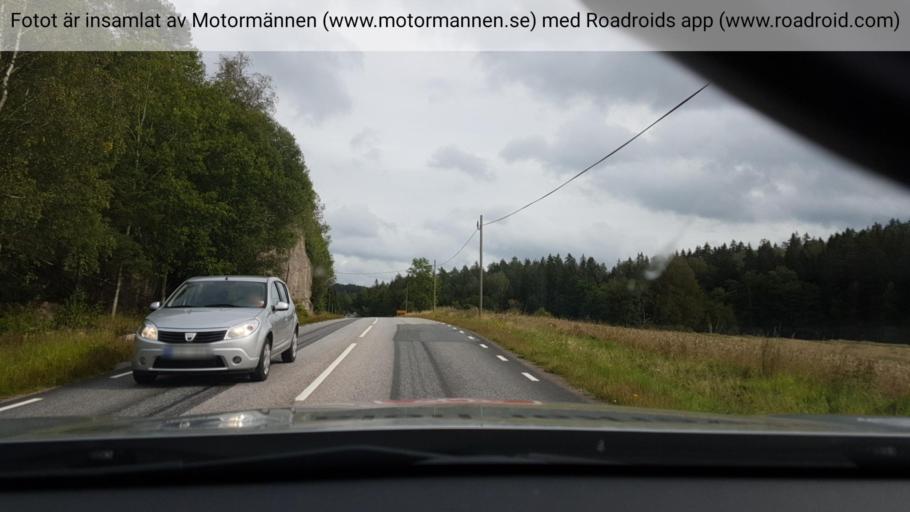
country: SE
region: Vaestra Goetaland
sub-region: Sotenas Kommun
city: Hunnebostrand
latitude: 58.5639
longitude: 11.3865
